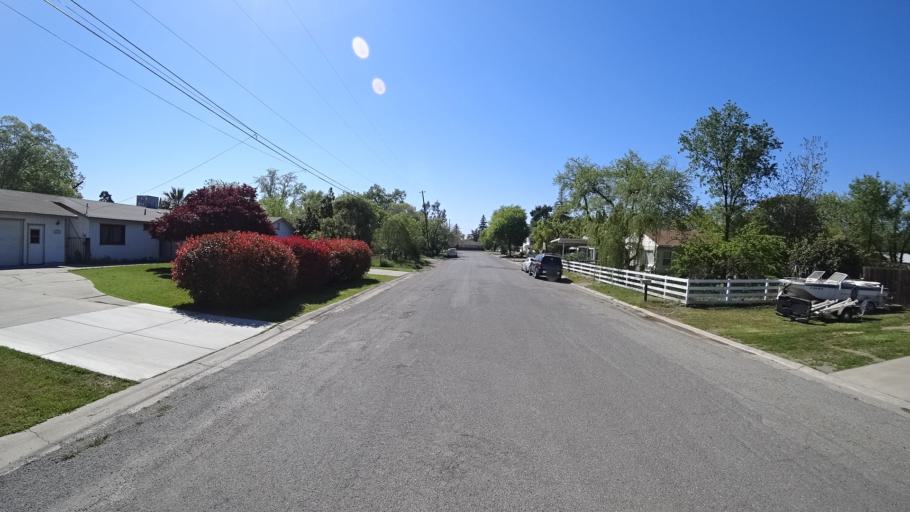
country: US
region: California
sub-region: Glenn County
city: Willows
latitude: 39.5254
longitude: -122.1881
